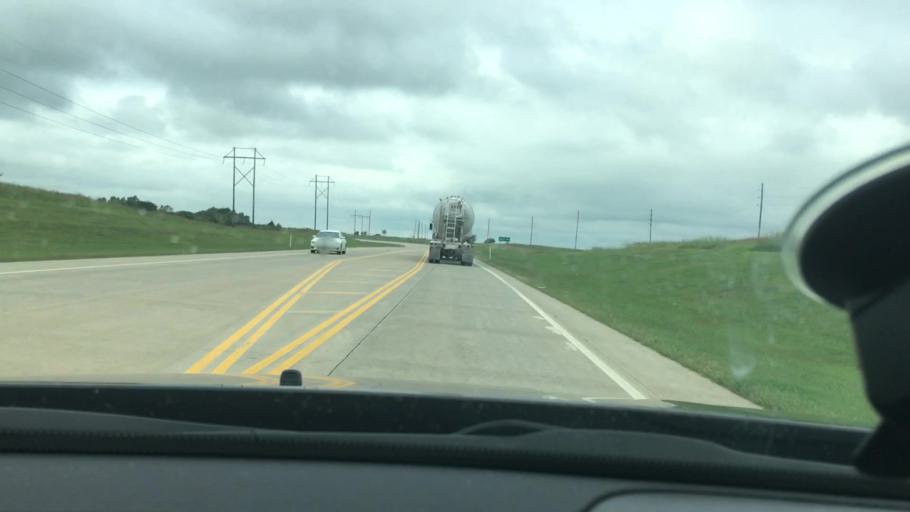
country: US
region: Oklahoma
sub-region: Pontotoc County
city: Ada
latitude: 34.6518
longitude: -96.8287
